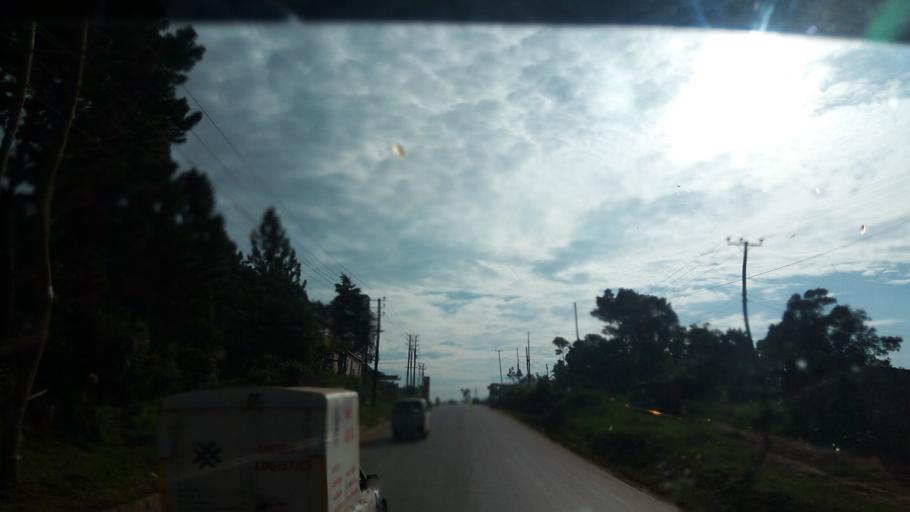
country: UG
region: Central Region
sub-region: Wakiso District
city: Wakiso
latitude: 0.4479
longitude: 32.5300
